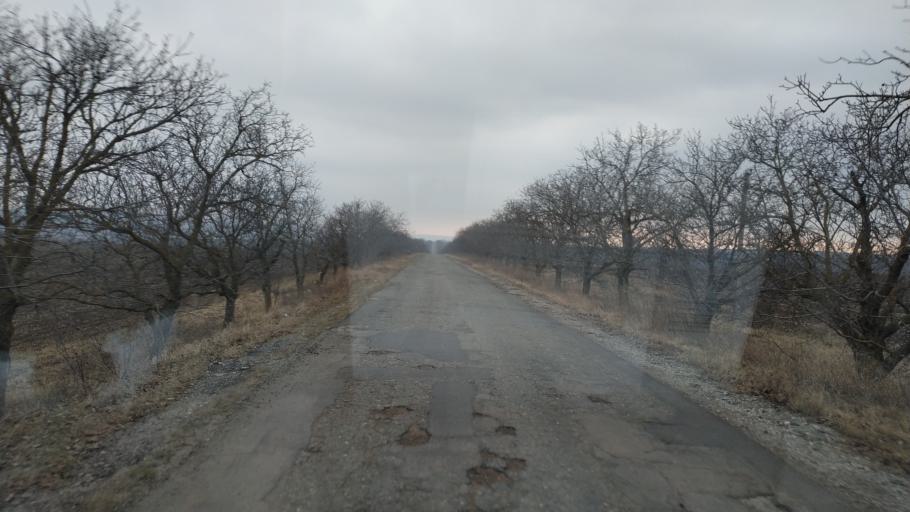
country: MD
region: Hincesti
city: Dancu
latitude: 46.8796
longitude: 28.2979
